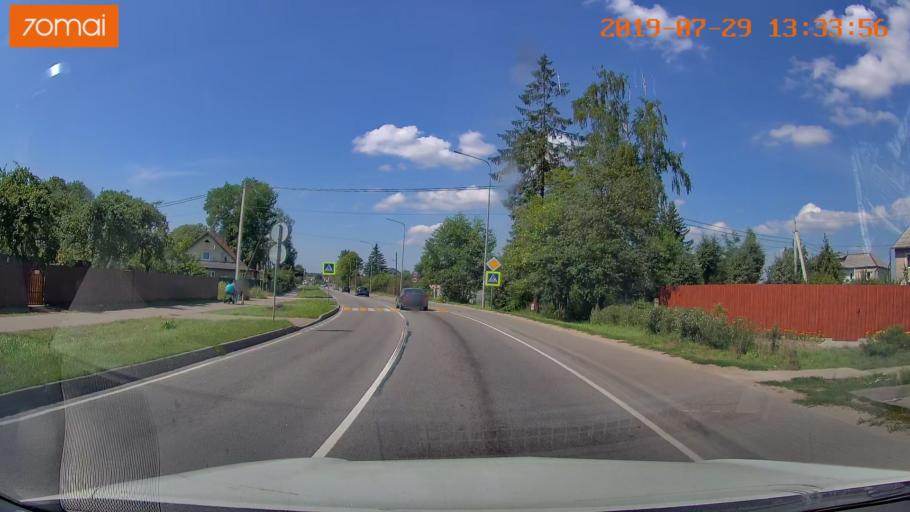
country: RU
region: Kaliningrad
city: Volochayevskoye
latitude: 54.6998
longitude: 20.2221
